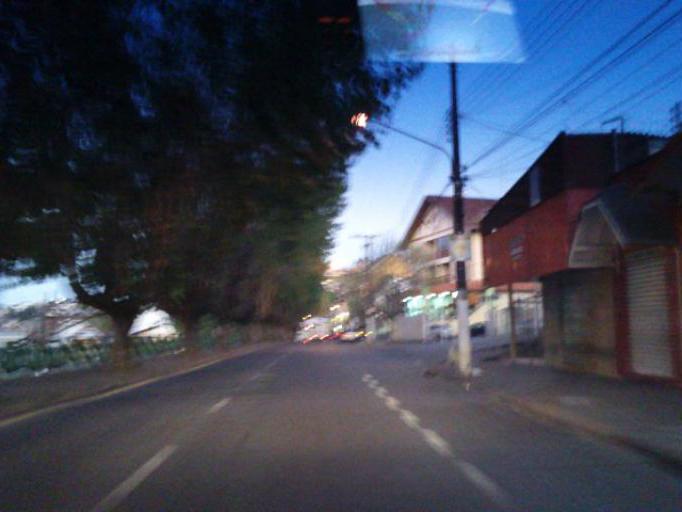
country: BR
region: Sao Paulo
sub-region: Campos Do Jordao
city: Campos do Jordao
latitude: -22.7362
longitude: -45.5894
